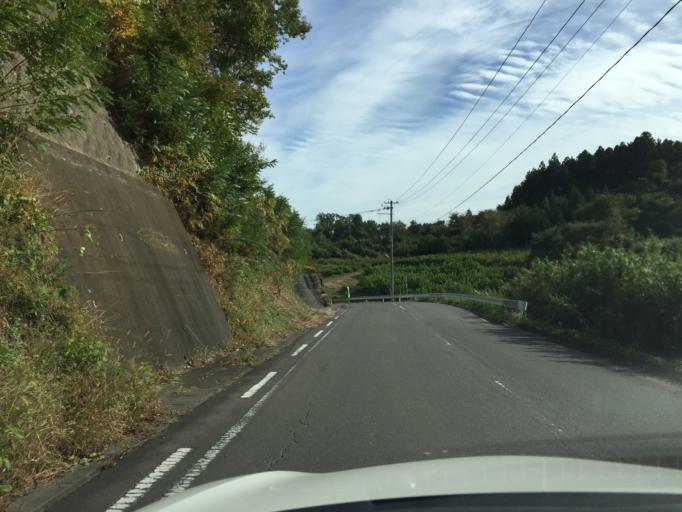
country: JP
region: Fukushima
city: Nihommatsu
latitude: 37.5792
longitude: 140.4805
